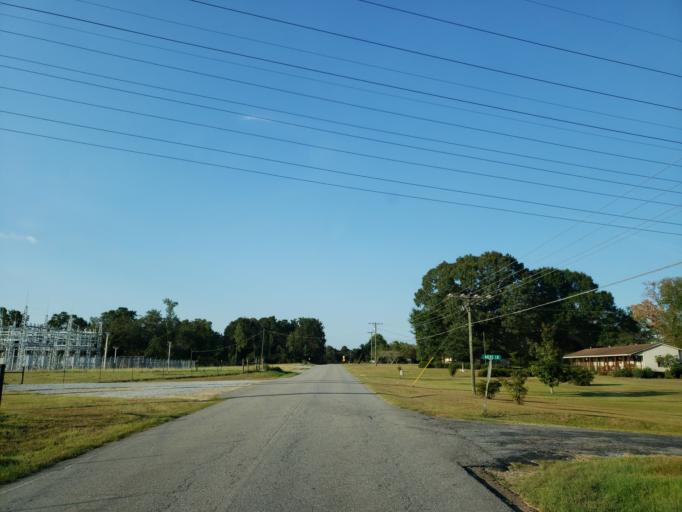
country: US
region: Mississippi
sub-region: Lamar County
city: West Hattiesburg
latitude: 31.3301
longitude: -89.4469
